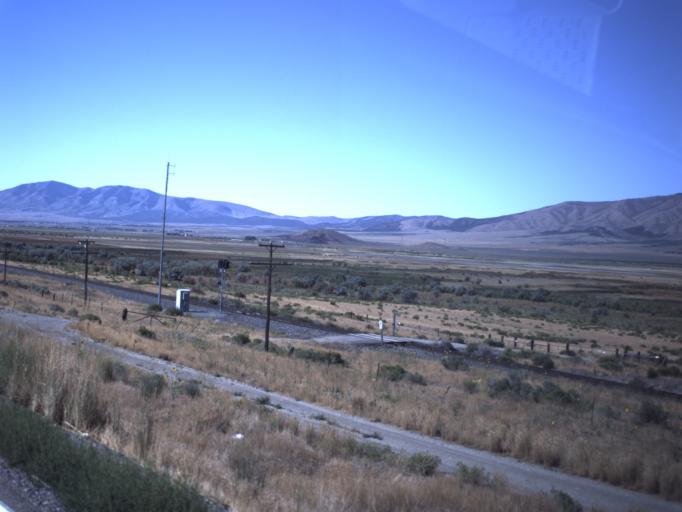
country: US
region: Utah
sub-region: Tooele County
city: Tooele
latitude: 40.4276
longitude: -112.3801
